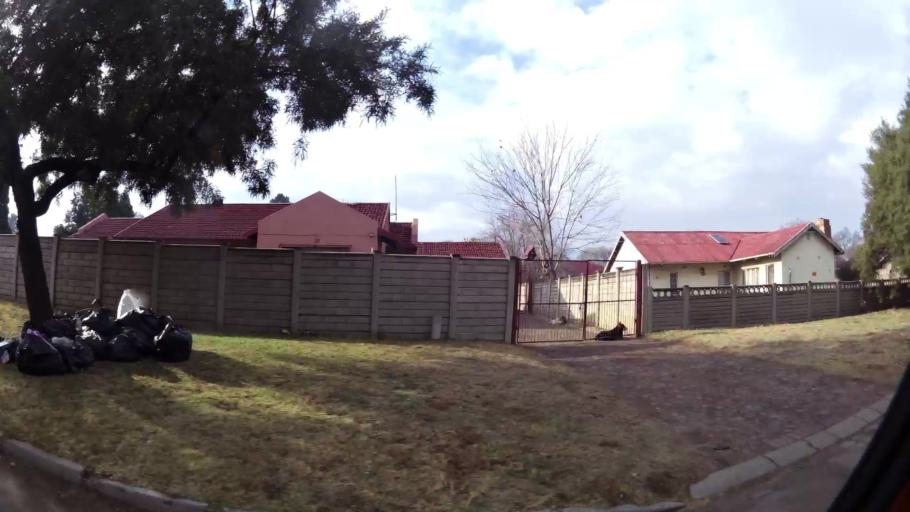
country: ZA
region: Gauteng
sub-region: Sedibeng District Municipality
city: Vanderbijlpark
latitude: -26.7039
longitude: 27.8180
